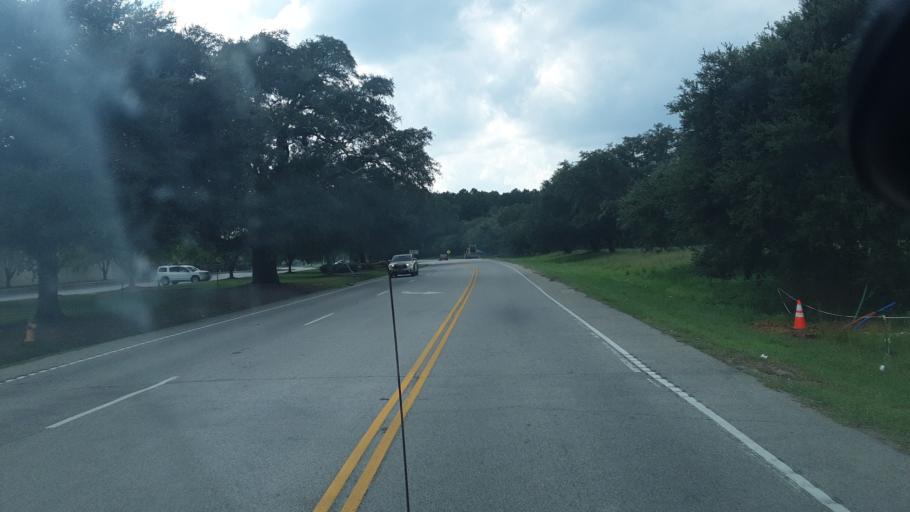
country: US
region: South Carolina
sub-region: Sumter County
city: Sumter
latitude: 33.9681
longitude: -80.3606
